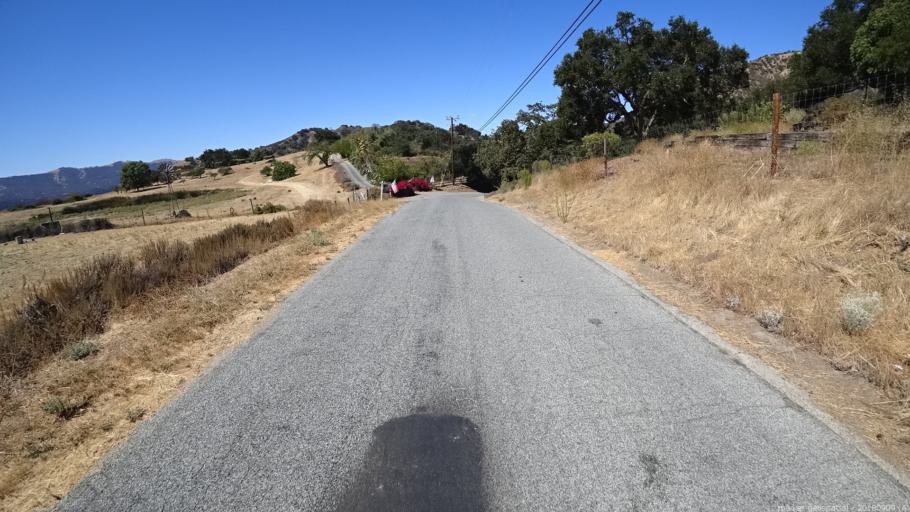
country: US
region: California
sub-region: Monterey County
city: Carmel Valley Village
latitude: 36.5419
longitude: -121.6614
